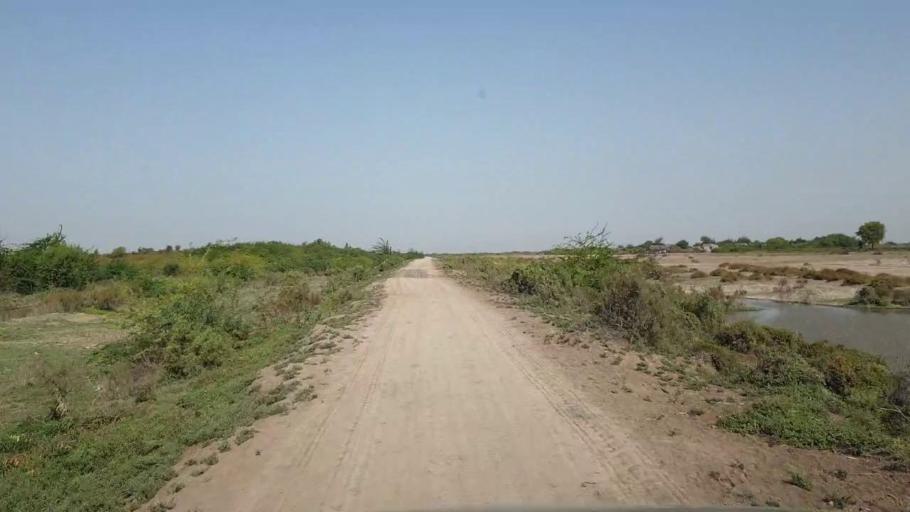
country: PK
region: Sindh
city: Tando Bago
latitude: 24.6471
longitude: 69.0717
